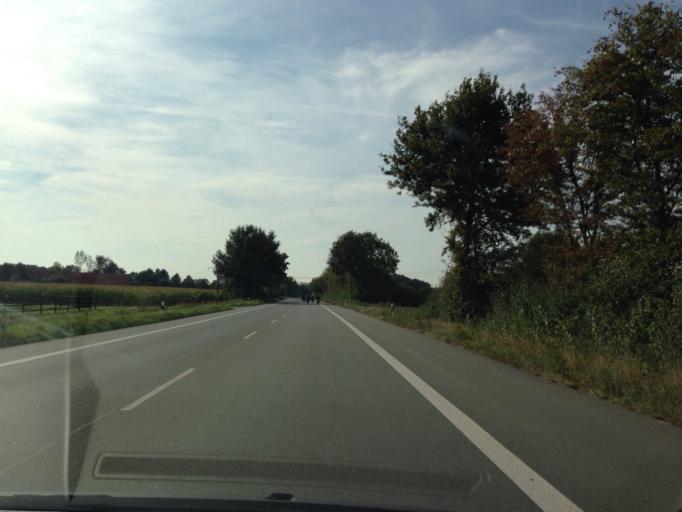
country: DE
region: North Rhine-Westphalia
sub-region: Regierungsbezirk Munster
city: Nordkirchen
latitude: 51.7857
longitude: 7.5197
